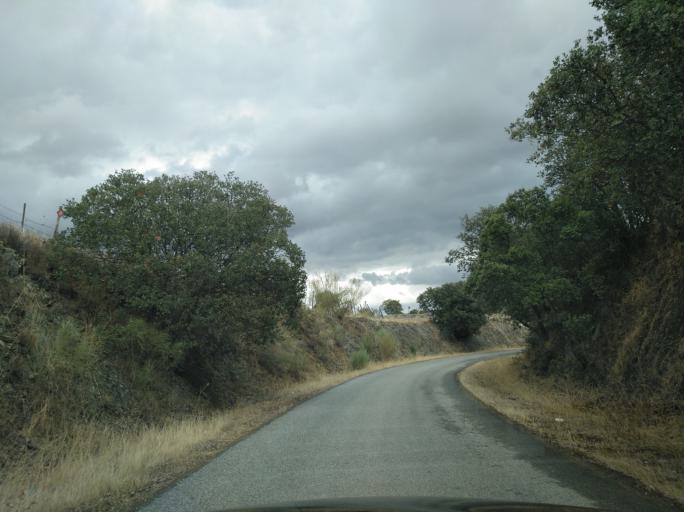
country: PT
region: Portalegre
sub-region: Campo Maior
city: Campo Maior
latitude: 39.0376
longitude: -7.1419
